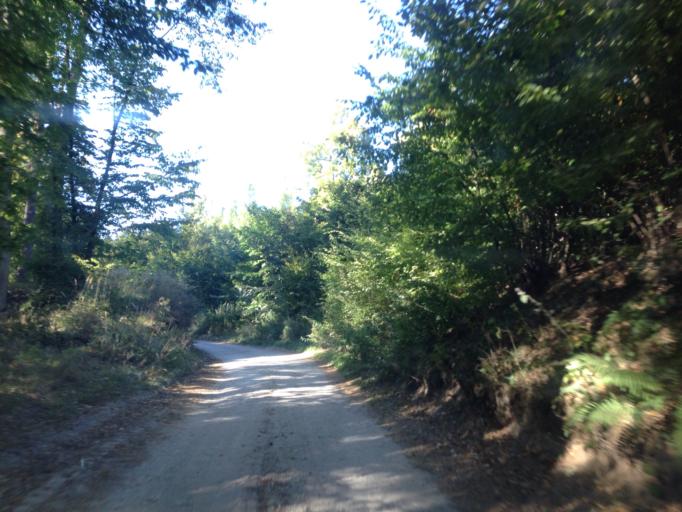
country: PL
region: Kujawsko-Pomorskie
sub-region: Powiat brodnicki
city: Gorzno
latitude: 53.2350
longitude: 19.6951
